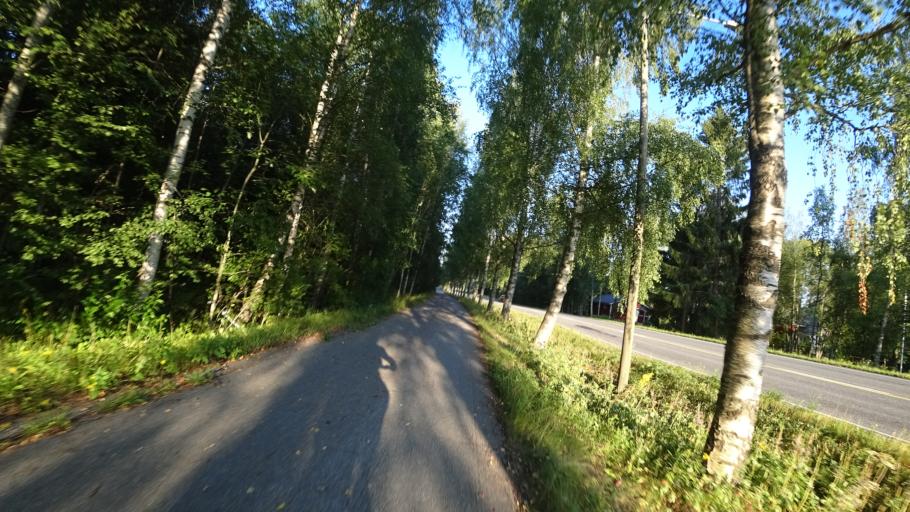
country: FI
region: Pirkanmaa
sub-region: Tampere
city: Nokia
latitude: 61.4714
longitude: 23.3853
